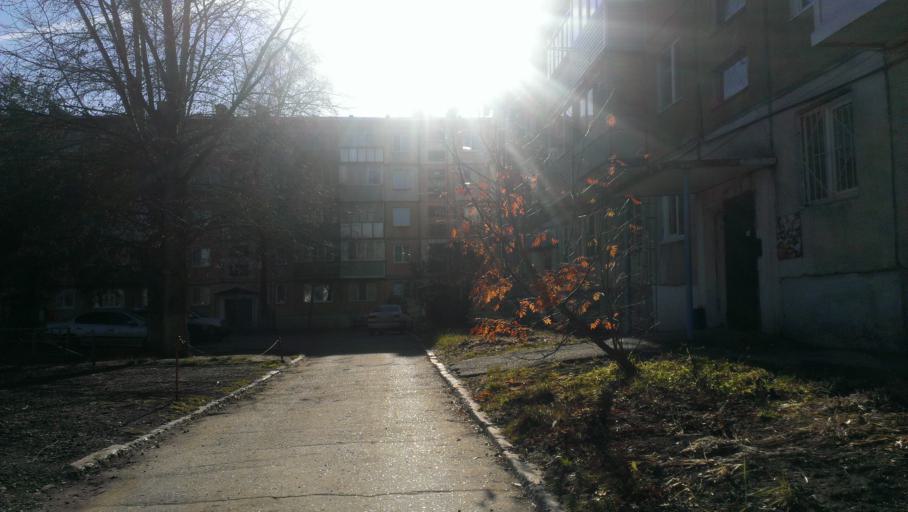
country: RU
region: Altai Krai
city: Novosilikatnyy
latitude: 53.3498
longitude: 83.6814
